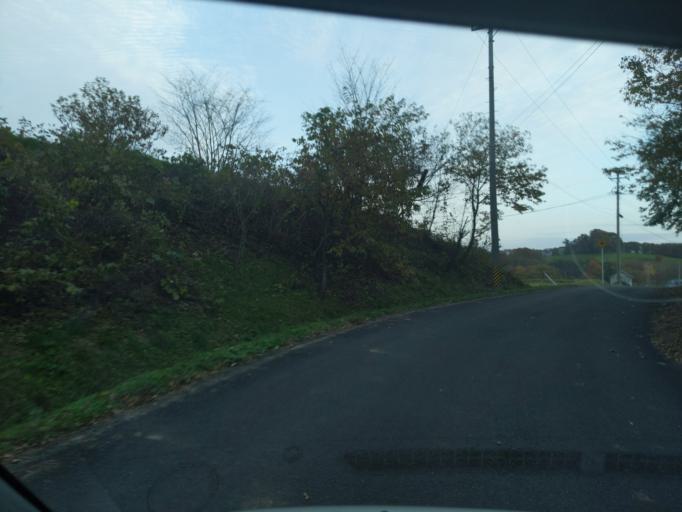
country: JP
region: Iwate
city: Ichinoseki
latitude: 38.9942
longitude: 141.0132
